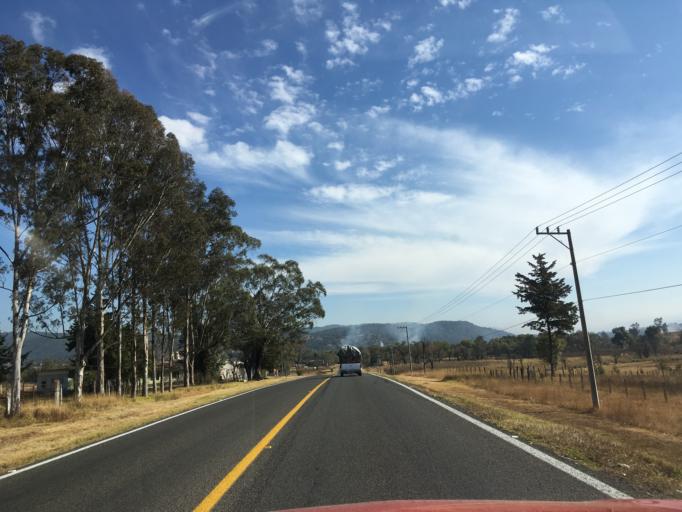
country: MX
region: Michoacan
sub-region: Hidalgo
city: Colonia Ecologica Asociacion de Lucha Social (Lucha Social)
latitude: 19.6926
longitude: -100.6189
